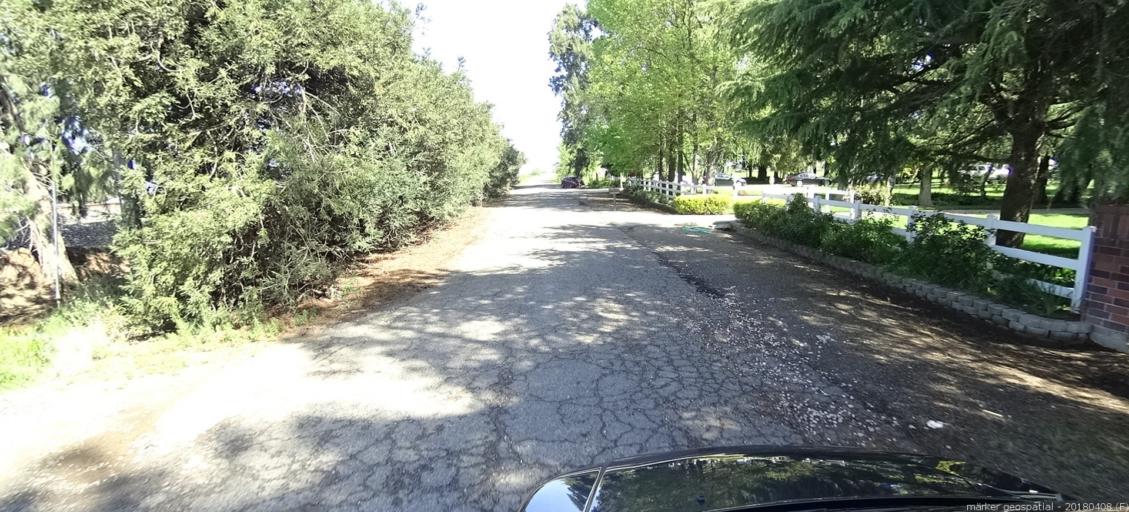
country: US
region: California
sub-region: Sacramento County
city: Laguna
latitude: 38.3275
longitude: -121.4448
